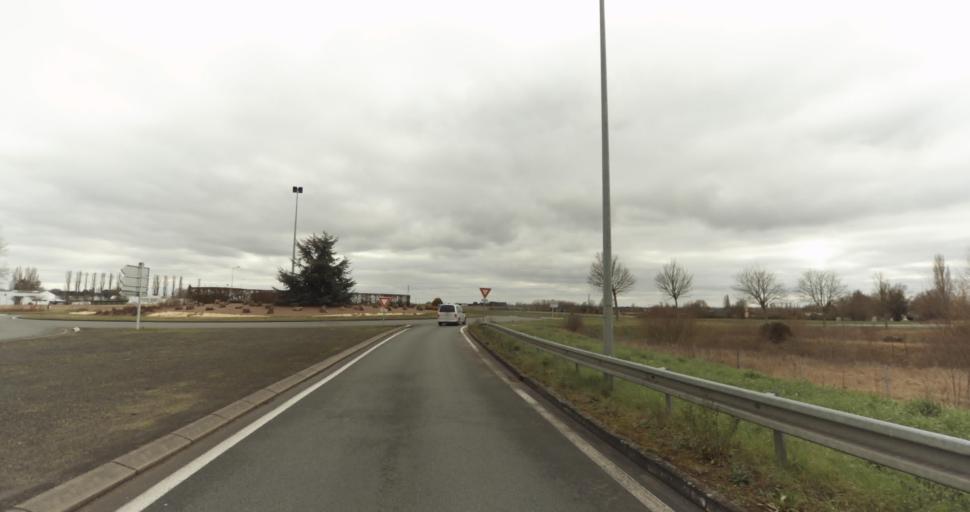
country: FR
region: Pays de la Loire
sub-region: Departement de Maine-et-Loire
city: Saint-Philbert-du-Peuple
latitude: 47.3713
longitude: -0.0996
